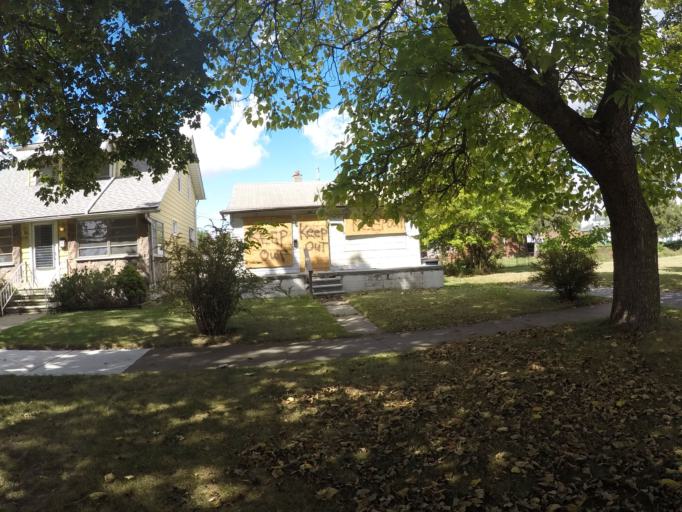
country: US
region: Michigan
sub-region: Wayne County
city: Melvindale
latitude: 42.2666
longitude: -83.1589
